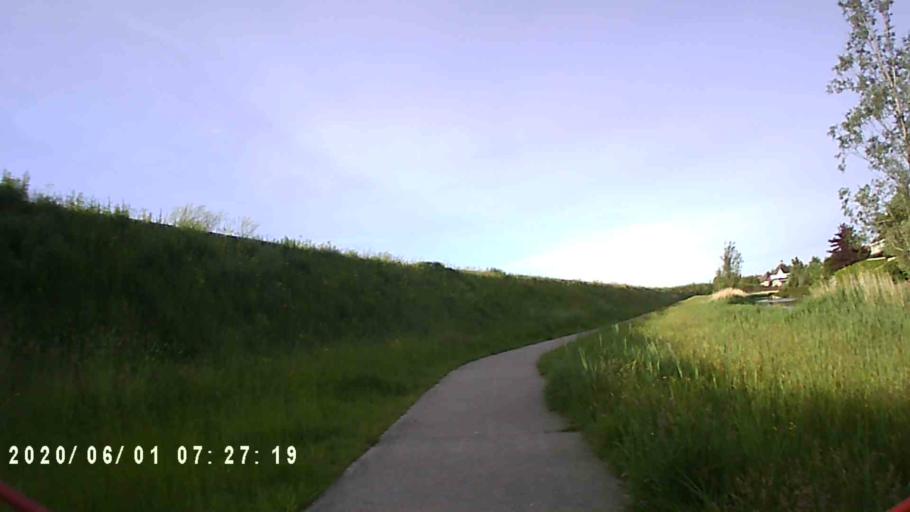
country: NL
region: Friesland
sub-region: Gemeente Dongeradeel
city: Dokkum
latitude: 53.3176
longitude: 6.0178
